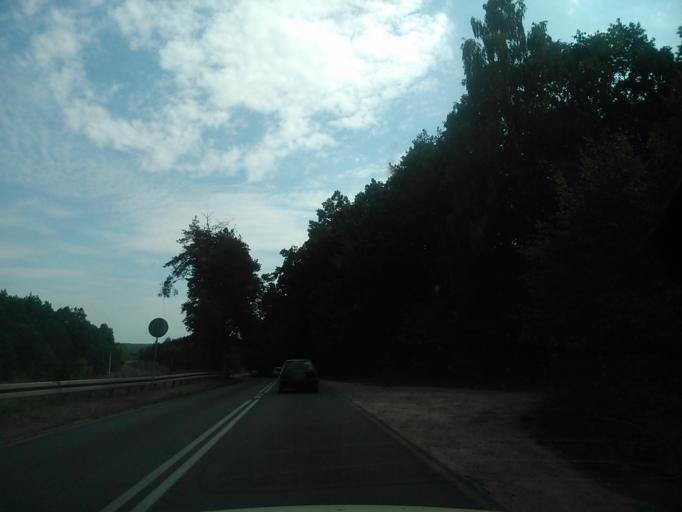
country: PL
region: Warmian-Masurian Voivodeship
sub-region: Powiat dzialdowski
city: Ilowo -Osada
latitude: 53.1574
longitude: 20.3123
